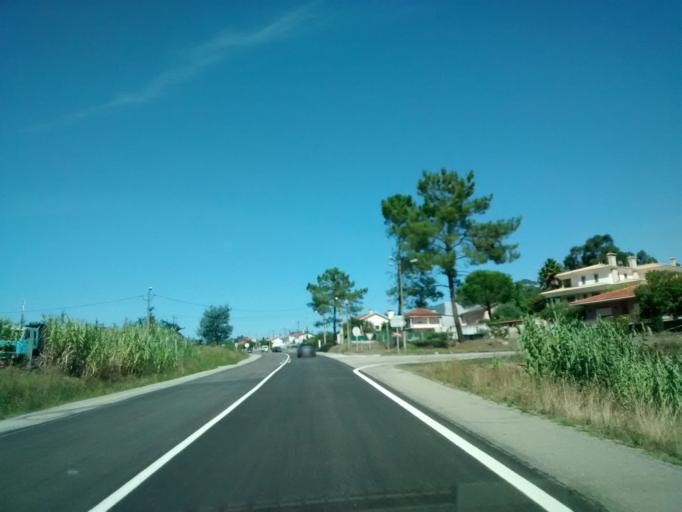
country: PT
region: Aveiro
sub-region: Oliveira do Bairro
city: Oia
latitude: 40.5359
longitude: -8.5145
